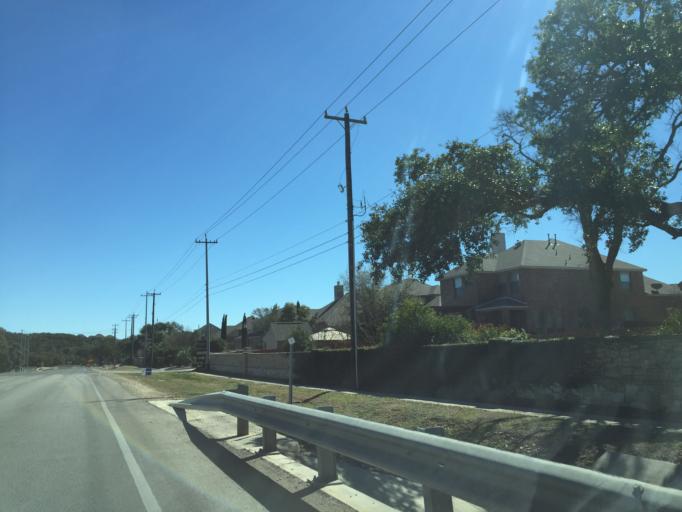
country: US
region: Texas
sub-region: Bexar County
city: Timberwood Park
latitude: 29.6888
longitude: -98.4466
